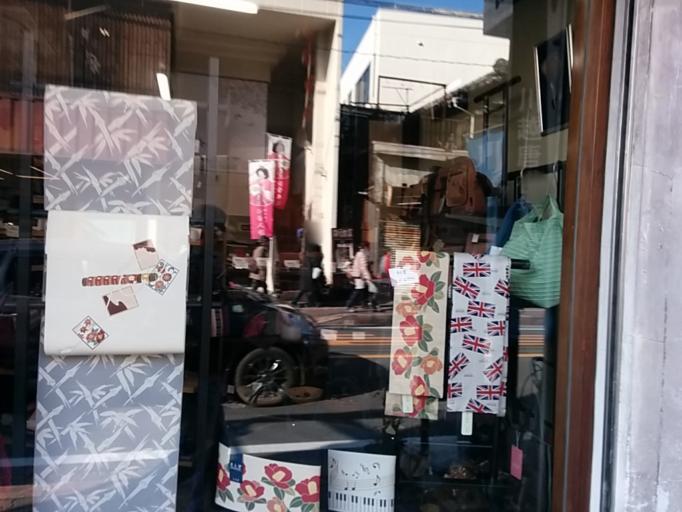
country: JP
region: Saitama
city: Kawagoe
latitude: 35.9208
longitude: 139.4828
